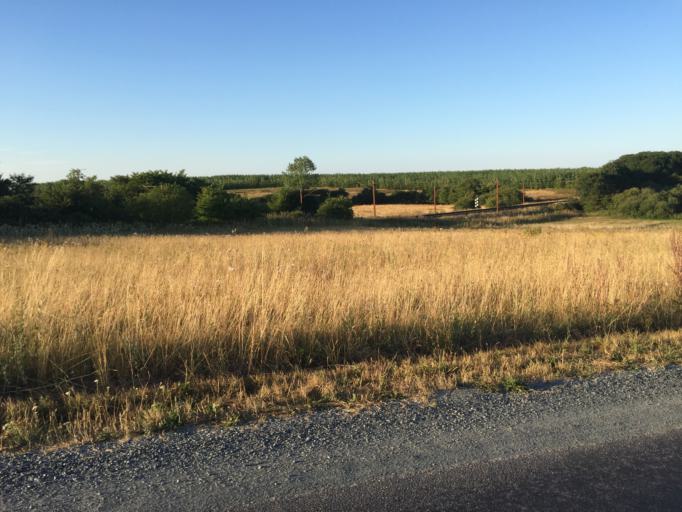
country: DK
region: South Denmark
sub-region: Odense Kommune
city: Bellinge
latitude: 55.3761
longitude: 10.3114
